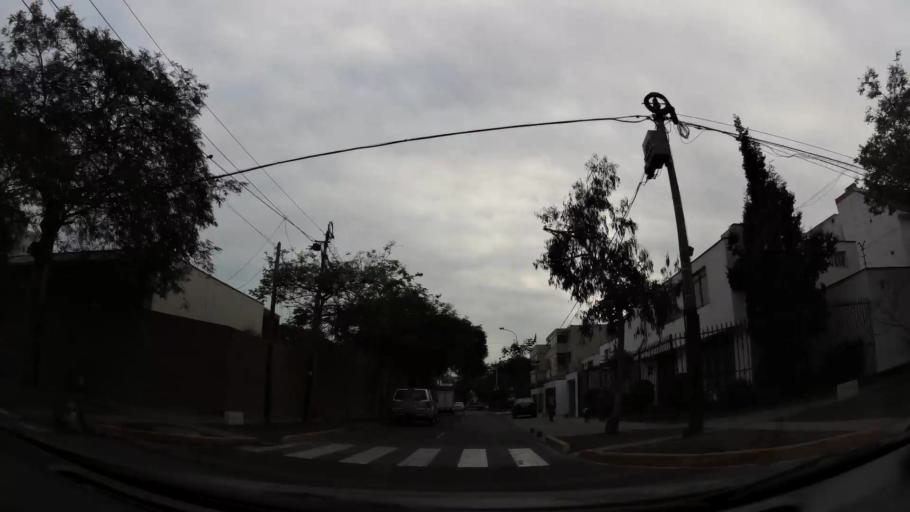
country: PE
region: Lima
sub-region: Lima
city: San Isidro
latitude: -12.1089
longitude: -77.0466
